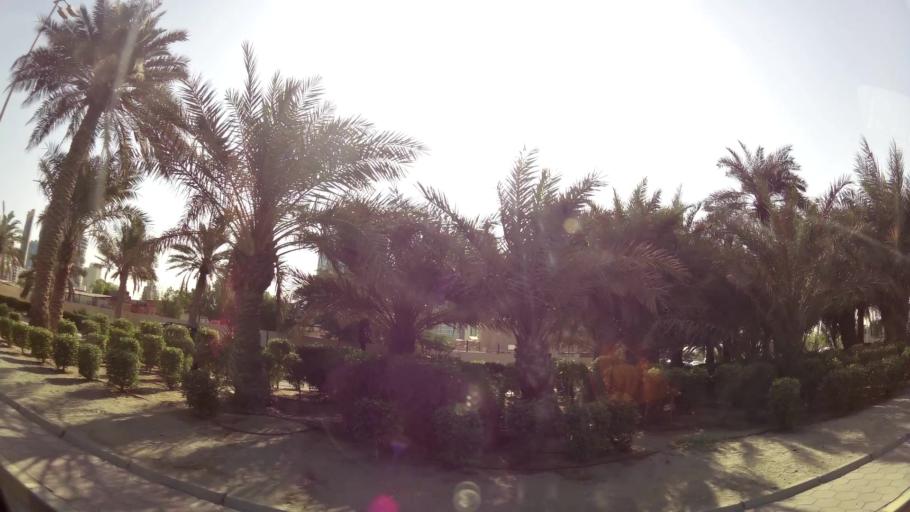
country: KW
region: Al Asimah
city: Ash Shamiyah
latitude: 29.3652
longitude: 47.9588
